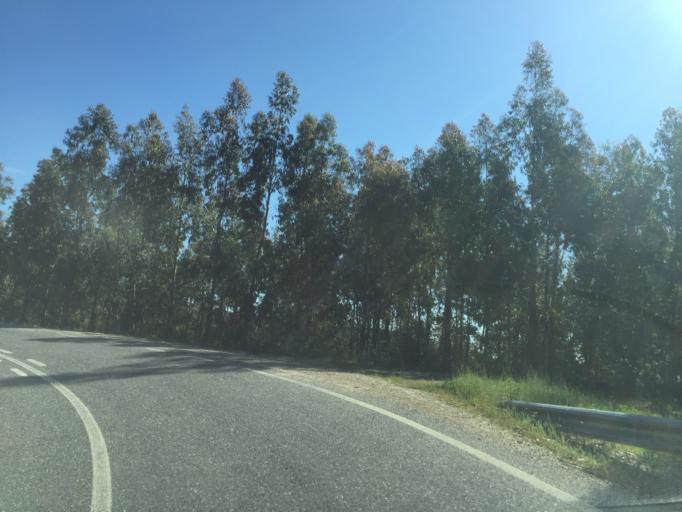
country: PT
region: Coimbra
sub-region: Pampilhosa da Serra
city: Pampilhosa da Serra
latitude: 40.0485
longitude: -7.8667
